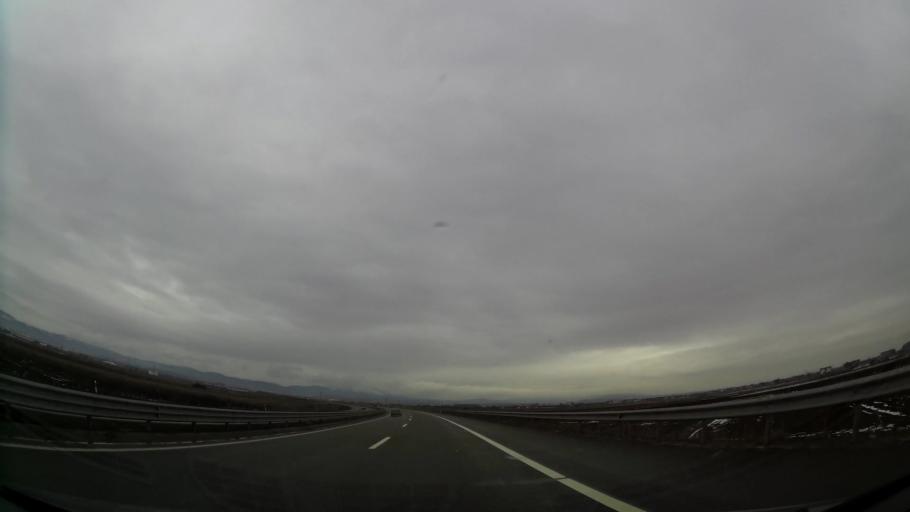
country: XK
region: Pristina
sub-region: Lipjan
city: Lipljan
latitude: 42.5313
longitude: 21.1417
